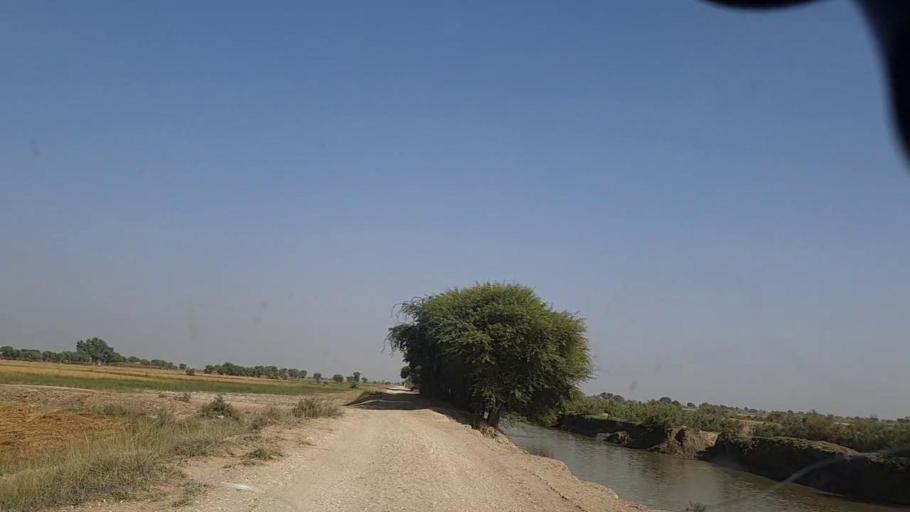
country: PK
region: Sindh
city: Rustam jo Goth
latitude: 28.0798
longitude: 68.8193
